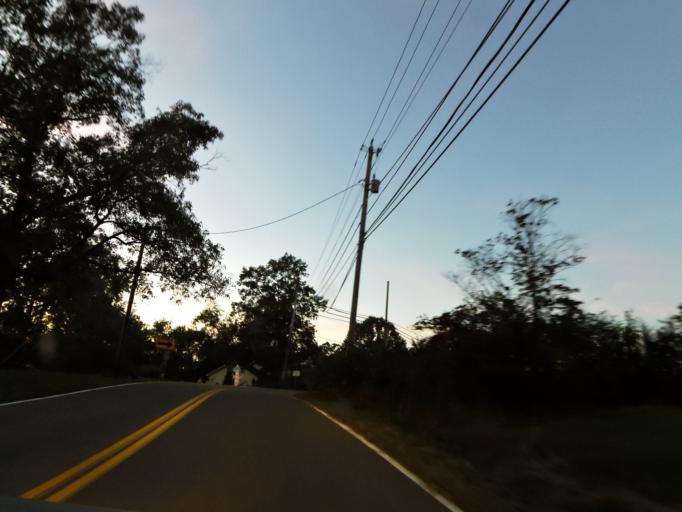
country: US
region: Tennessee
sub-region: Knox County
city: Mascot
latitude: 36.0102
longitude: -83.6410
